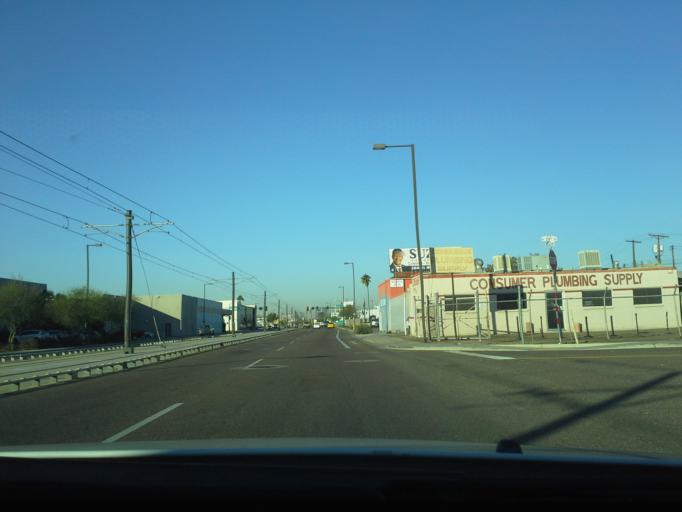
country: US
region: Arizona
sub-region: Maricopa County
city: Phoenix
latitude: 33.4483
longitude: -112.0192
